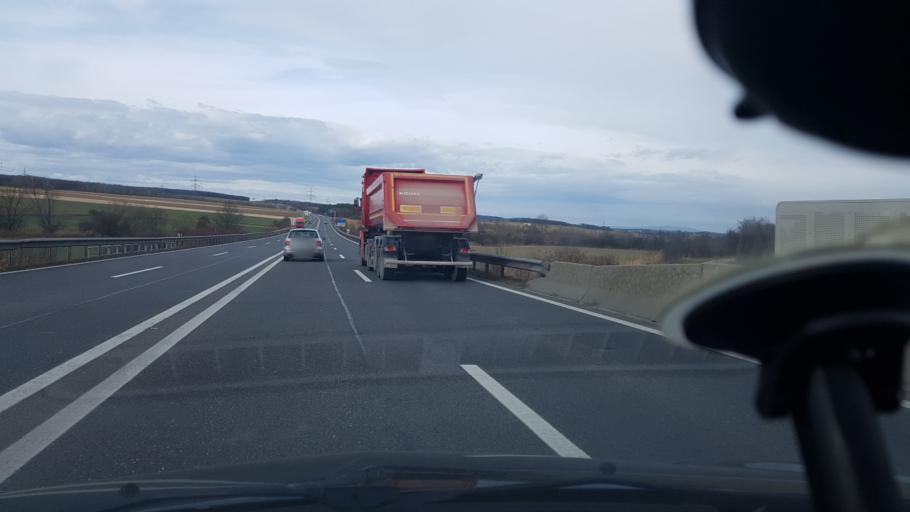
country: AT
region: Burgenland
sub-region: Politischer Bezirk Mattersburg
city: Mattersburg
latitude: 47.7603
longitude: 16.3979
